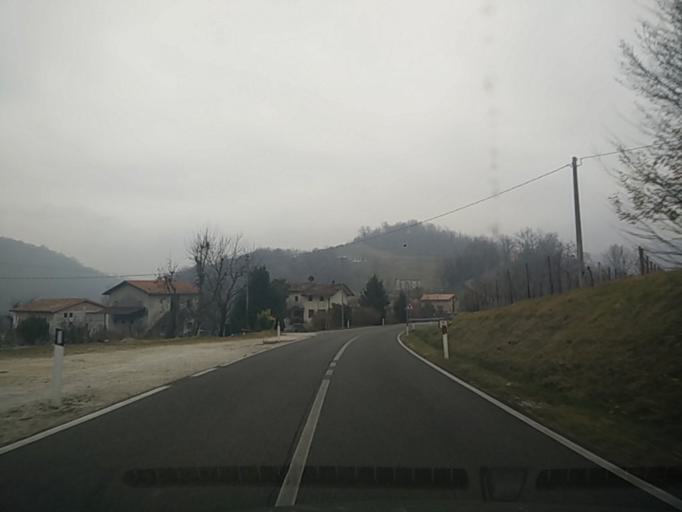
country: IT
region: Veneto
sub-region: Provincia di Treviso
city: Tarzo
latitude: 45.9677
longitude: 12.2299
